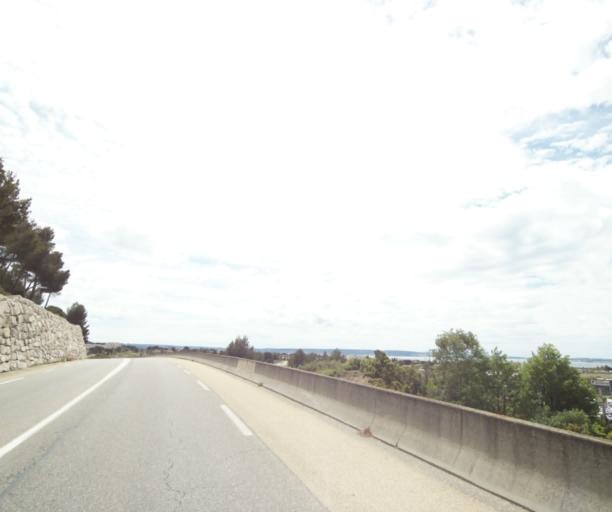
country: FR
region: Provence-Alpes-Cote d'Azur
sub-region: Departement des Bouches-du-Rhone
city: Rognac
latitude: 43.4966
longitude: 5.2309
